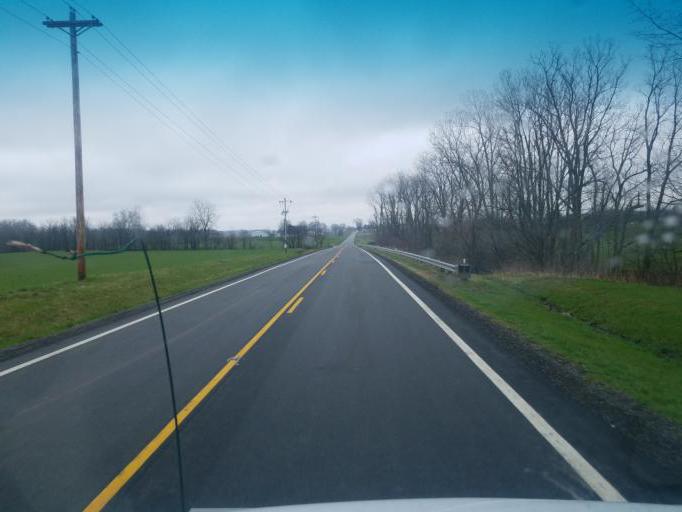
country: US
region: Ohio
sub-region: Huron County
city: Willard
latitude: 40.9601
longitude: -82.7901
